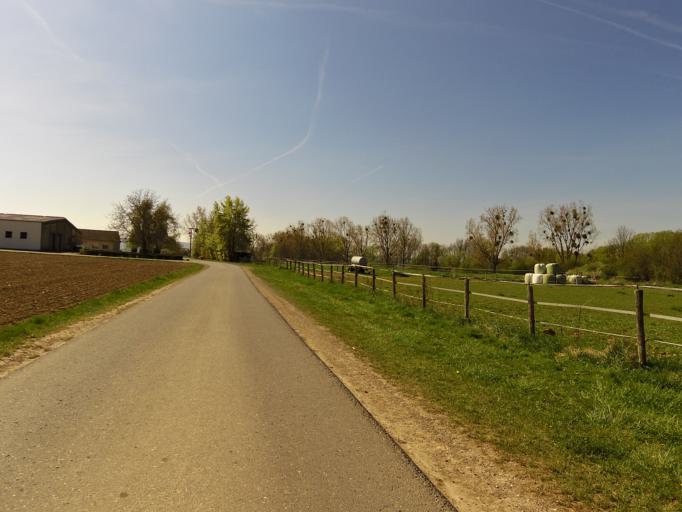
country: DE
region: North Rhine-Westphalia
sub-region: Regierungsbezirk Koln
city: Rheinbach
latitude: 50.6377
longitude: 6.8756
